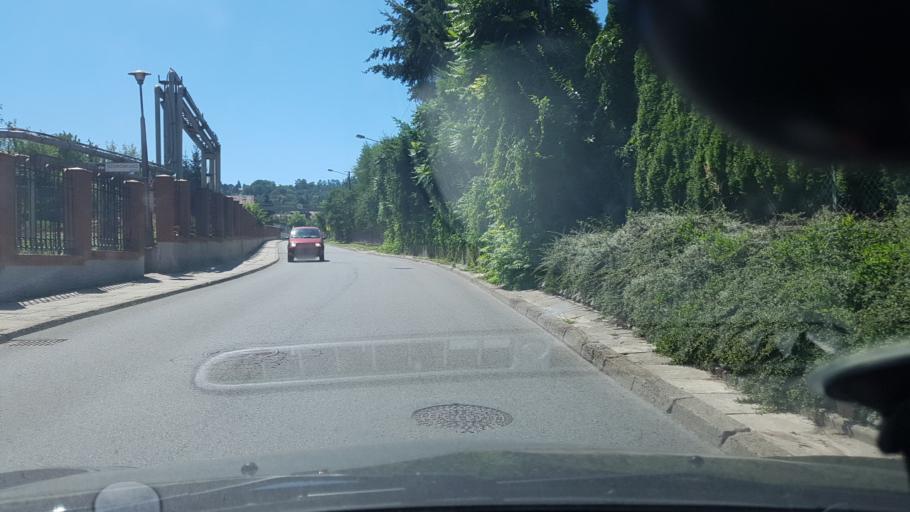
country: PL
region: Lesser Poland Voivodeship
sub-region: Powiat wielicki
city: Wieliczka
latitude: 49.9833
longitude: 20.0499
